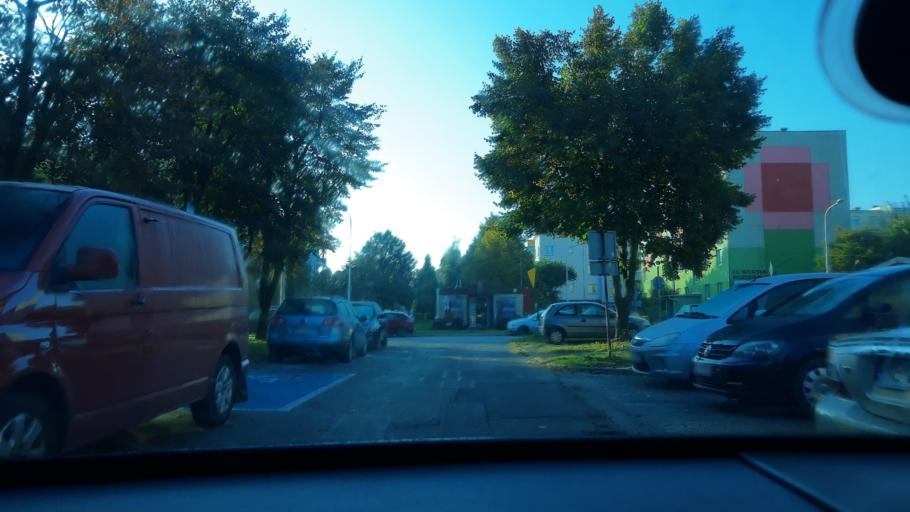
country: PL
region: Lodz Voivodeship
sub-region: Powiat sieradzki
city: Sieradz
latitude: 51.5927
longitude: 18.7108
